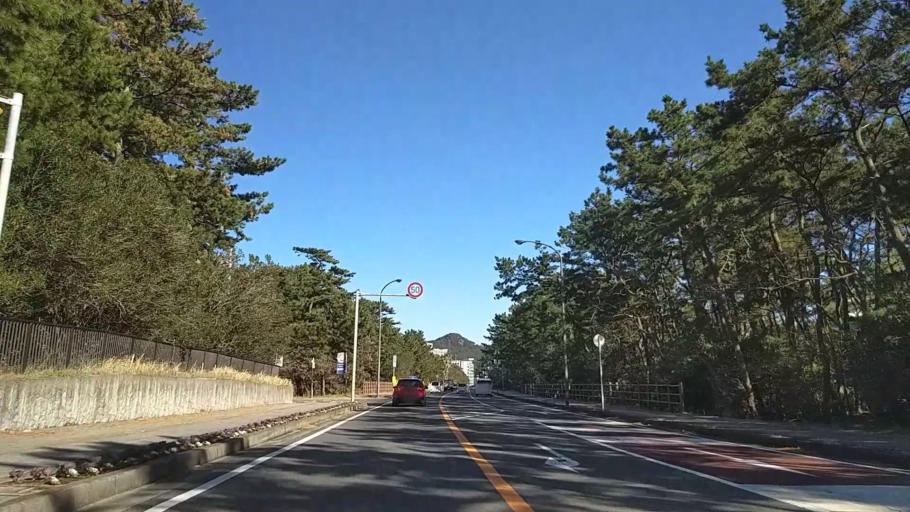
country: JP
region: Chiba
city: Kawaguchi
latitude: 35.1152
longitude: 140.1180
